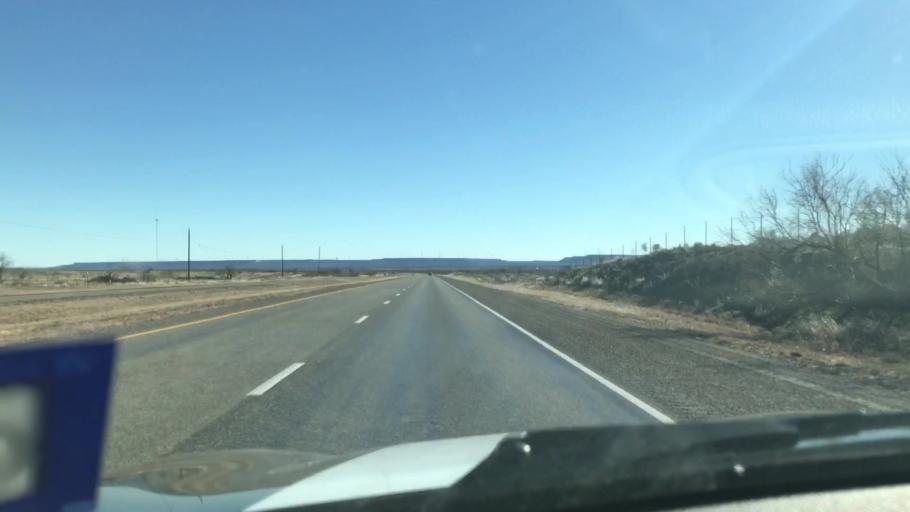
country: US
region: Texas
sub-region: Garza County
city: Post
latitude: 33.0804
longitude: -101.2403
